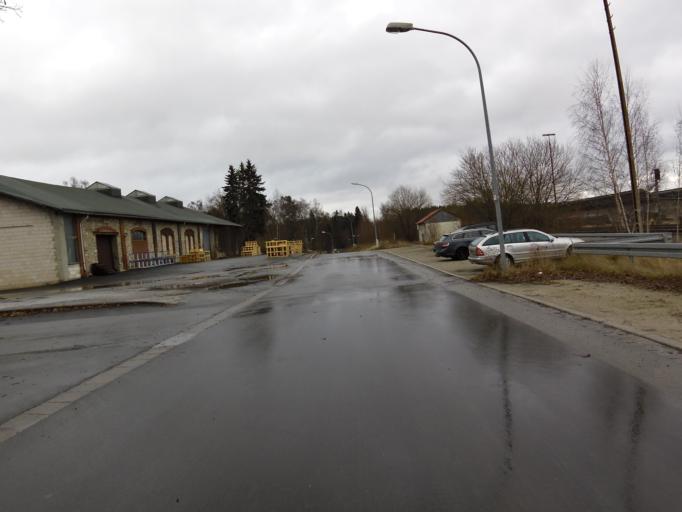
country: DE
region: Bavaria
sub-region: Upper Franconia
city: Wunsiedel
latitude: 50.0493
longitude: 12.0361
